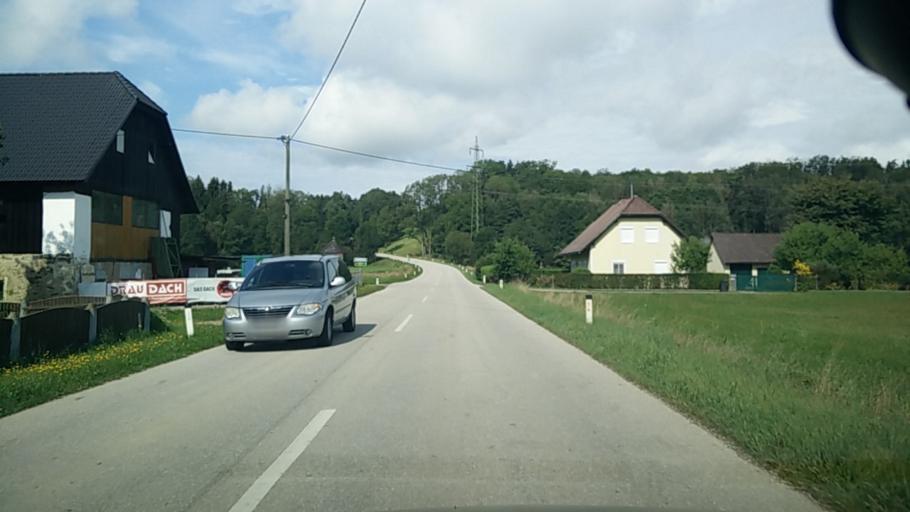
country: AT
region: Carinthia
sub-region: Politischer Bezirk Volkermarkt
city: Gallizien
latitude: 46.6241
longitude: 14.5439
